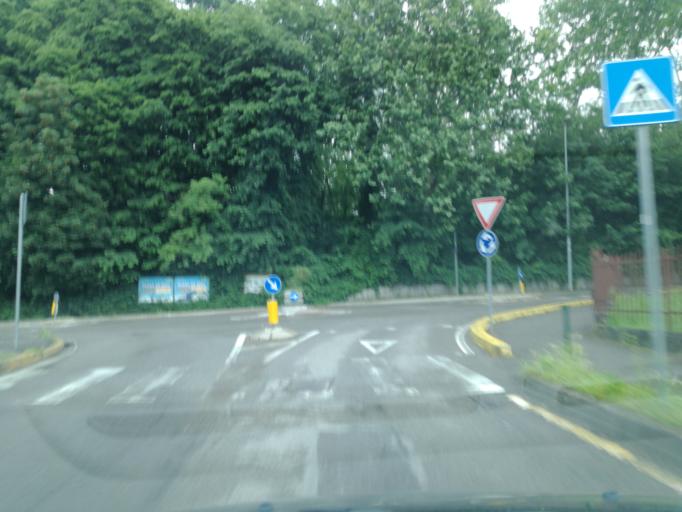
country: IT
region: Lombardy
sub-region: Provincia di Monza e Brianza
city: Carnate
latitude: 45.6538
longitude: 9.3779
